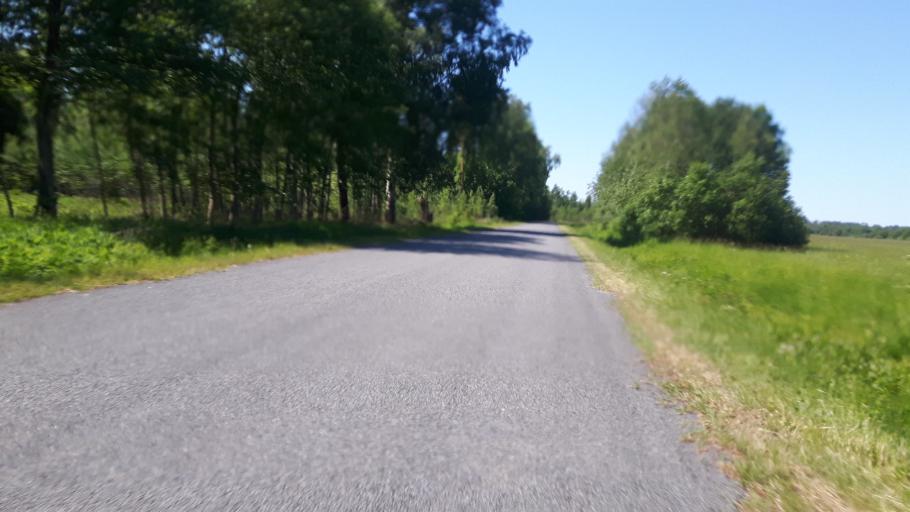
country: EE
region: Paernumaa
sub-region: Vaendra vald (alev)
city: Vandra
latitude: 58.5646
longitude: 24.9732
